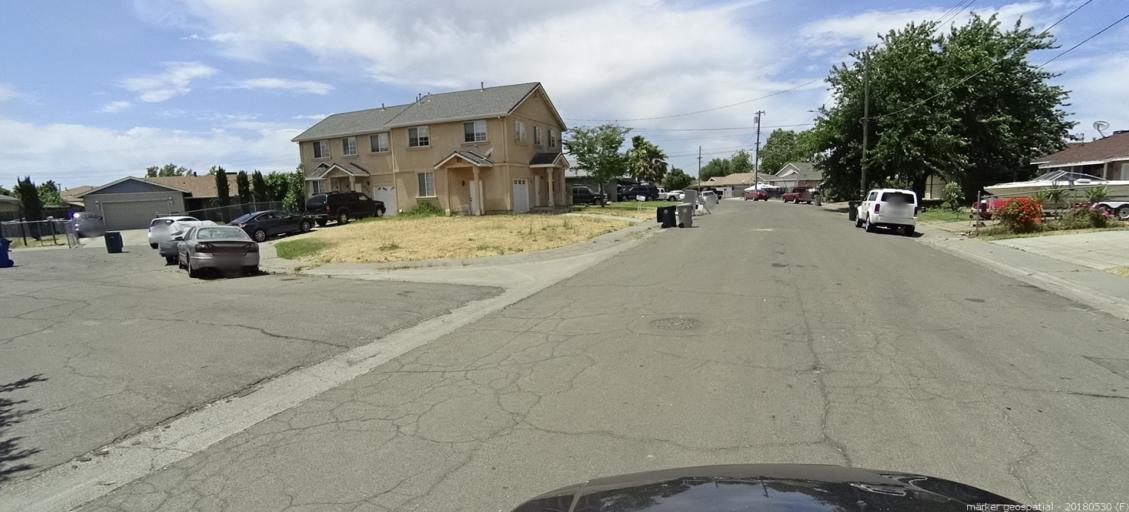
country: US
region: California
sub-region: Sacramento County
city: Sacramento
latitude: 38.6276
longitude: -121.4669
